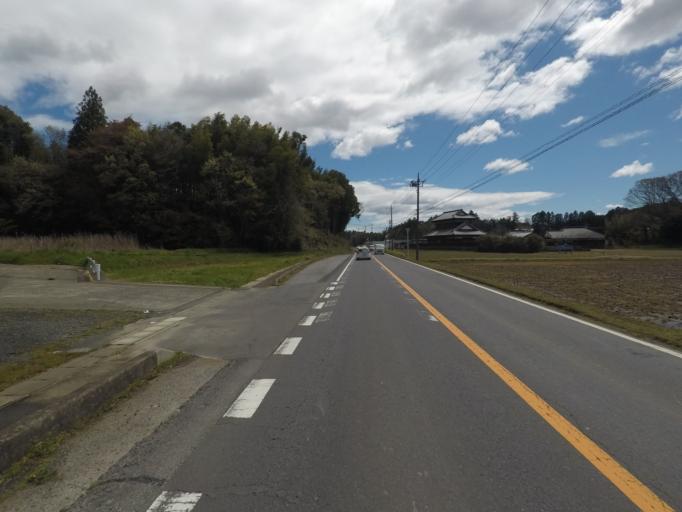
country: JP
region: Ibaraki
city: Okunoya
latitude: 36.1082
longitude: 140.4700
